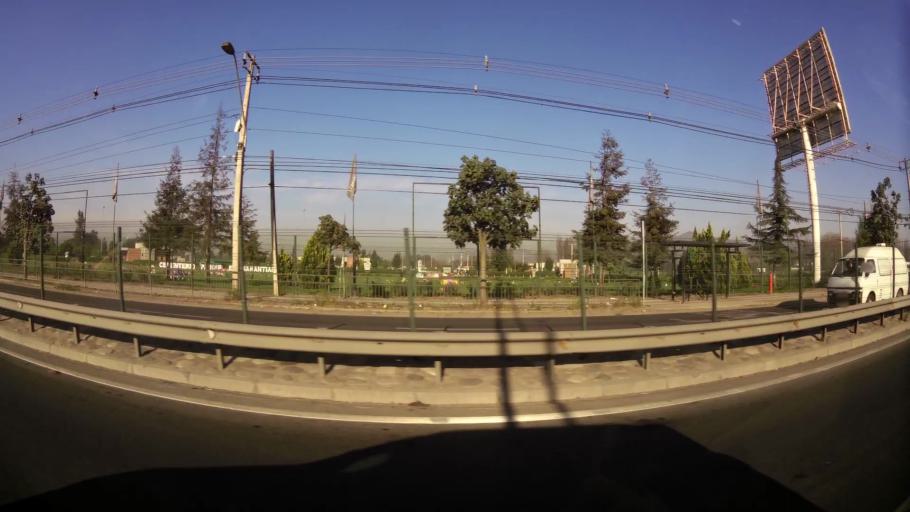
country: CL
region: Santiago Metropolitan
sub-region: Provincia de Santiago
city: Lo Prado
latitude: -33.4728
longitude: -70.7596
